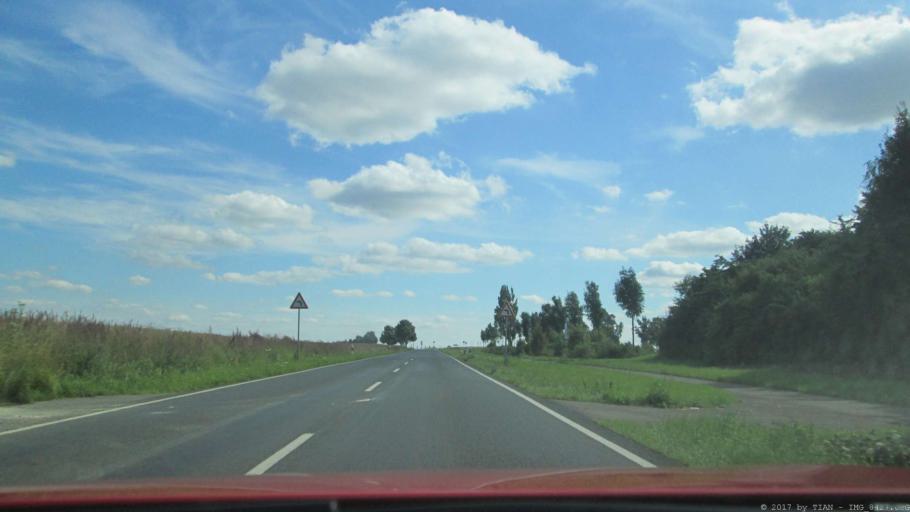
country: DE
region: Lower Saxony
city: Danndorf
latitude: 52.4101
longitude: 10.8478
